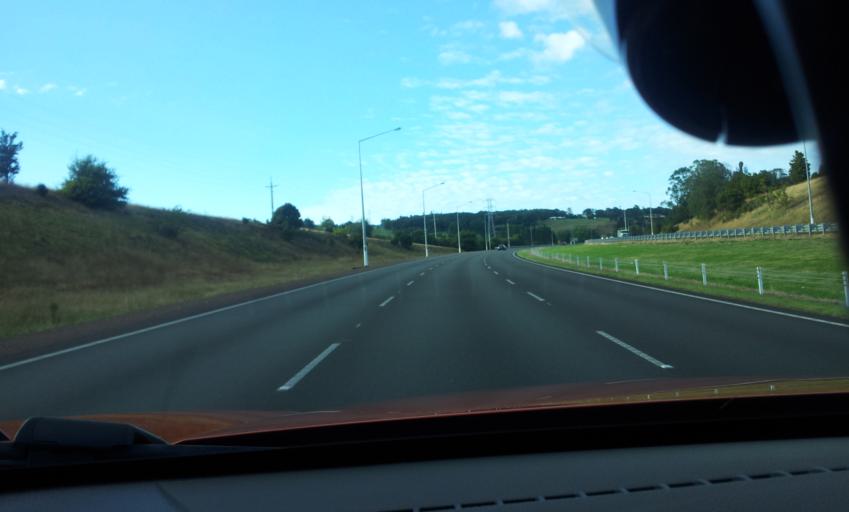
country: NZ
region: Auckland
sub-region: Auckland
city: Pukekohe East
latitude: -37.1660
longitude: 174.9840
